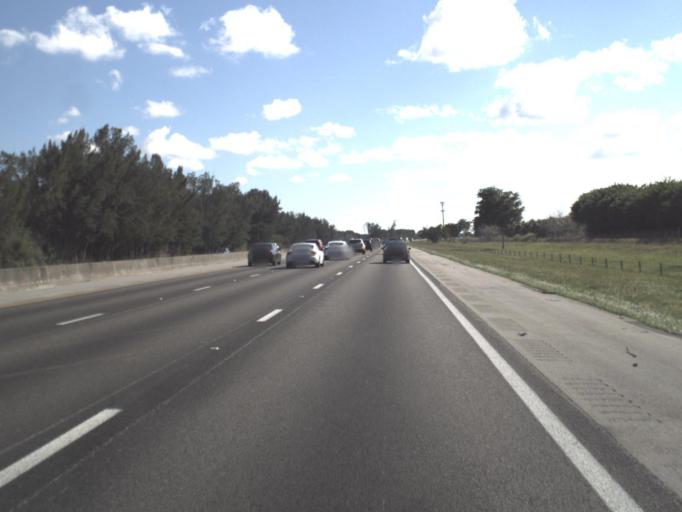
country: US
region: Florida
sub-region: Palm Beach County
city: Villages of Oriole
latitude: 26.4348
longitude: -80.1736
